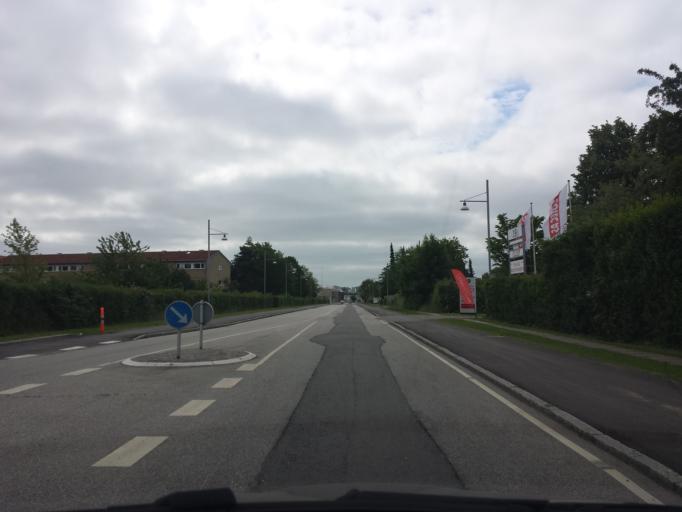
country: DK
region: Capital Region
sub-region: Albertslund Kommune
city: Albertslund
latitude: 55.6675
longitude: 12.3714
